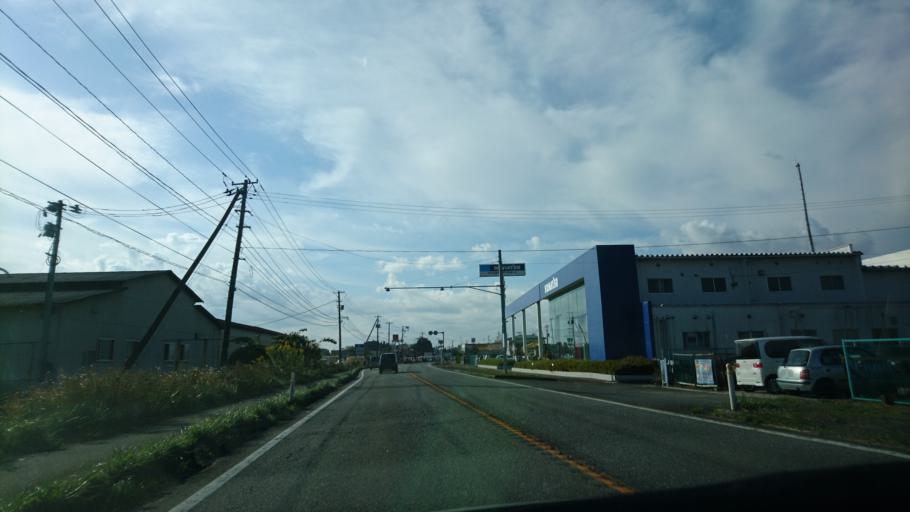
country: JP
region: Miyagi
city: Furukawa
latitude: 38.6098
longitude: 140.9829
